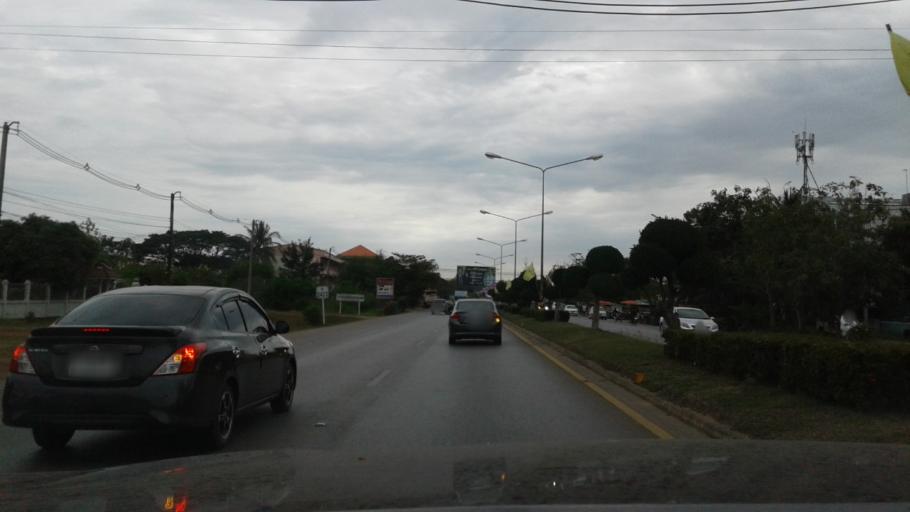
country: TH
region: Changwat Udon Thani
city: Udon Thani
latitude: 17.3887
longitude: 102.7672
